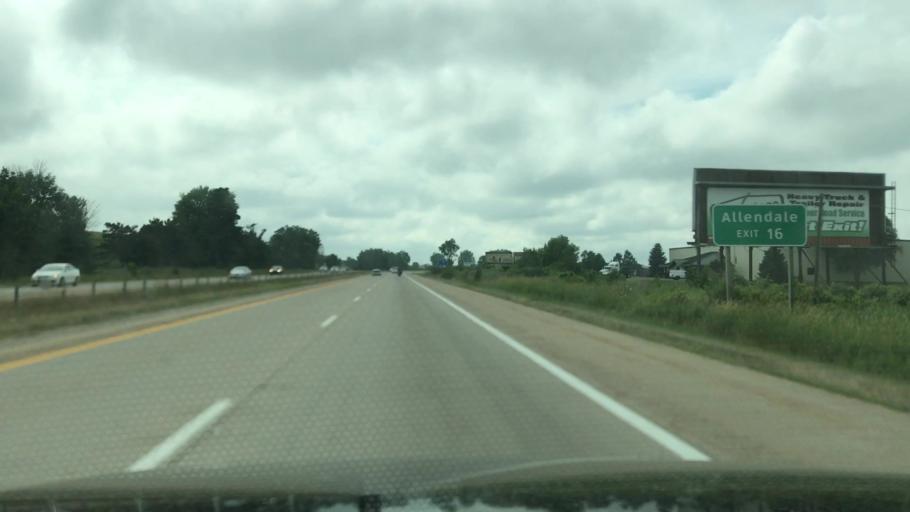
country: US
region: Michigan
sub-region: Ottawa County
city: Coopersville
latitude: 43.0529
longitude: -85.9415
